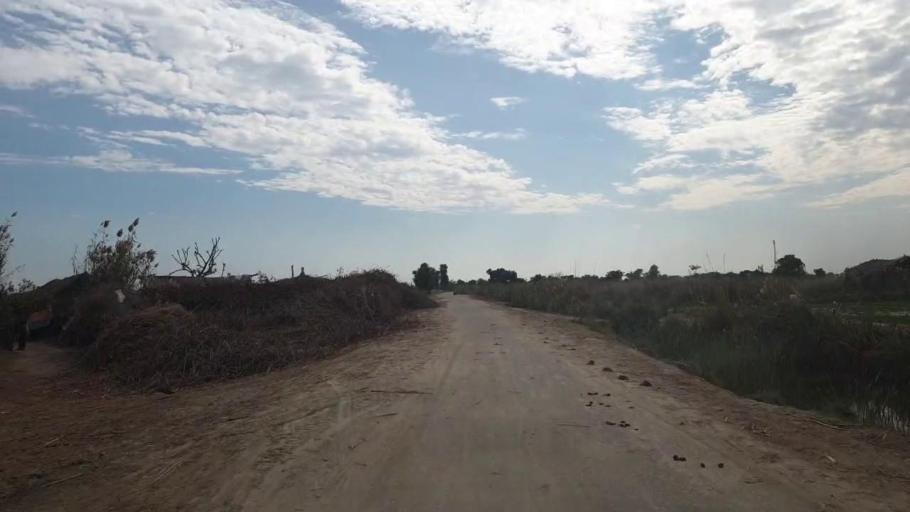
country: PK
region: Sindh
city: Jhol
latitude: 25.9934
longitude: 68.8977
